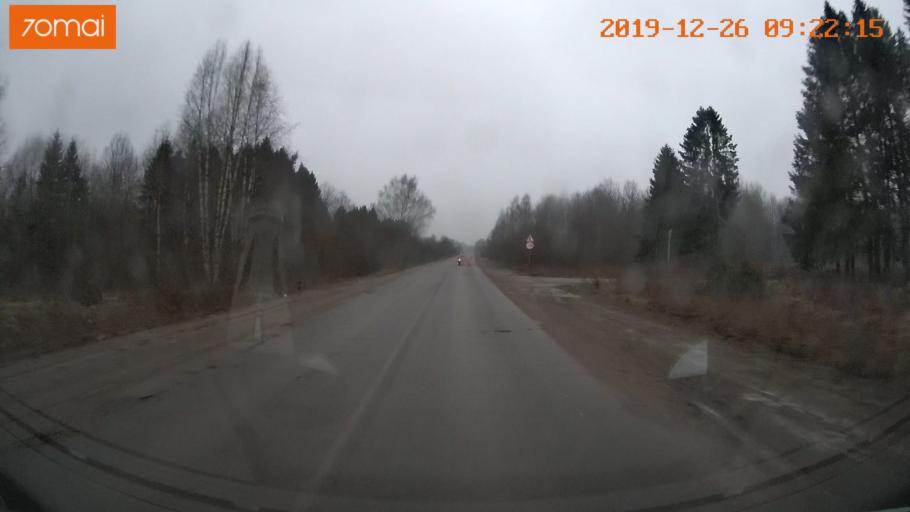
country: RU
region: Vologda
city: Gryazovets
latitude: 58.9783
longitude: 40.2176
